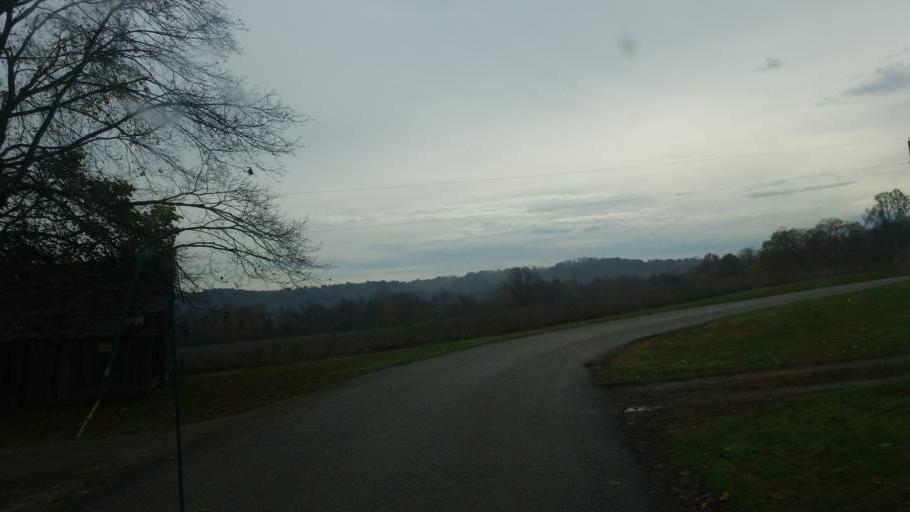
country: US
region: Ohio
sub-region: Washington County
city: Beverly
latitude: 39.5333
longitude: -81.7383
